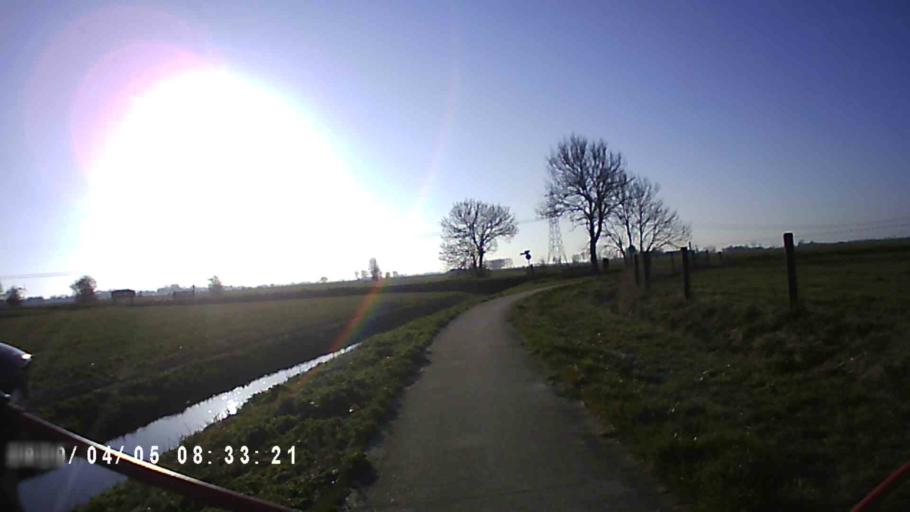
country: NL
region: Groningen
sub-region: Gemeente Winsum
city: Winsum
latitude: 53.3257
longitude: 6.4912
